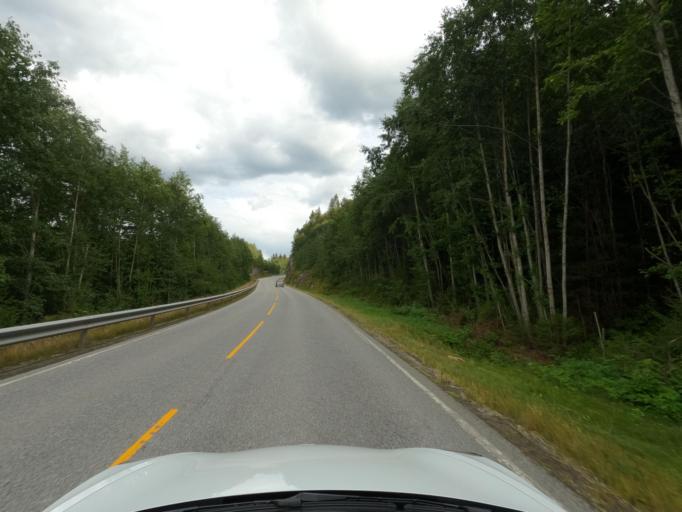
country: NO
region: Telemark
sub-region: Hjartdal
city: Sauland
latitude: 59.8341
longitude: 8.9657
